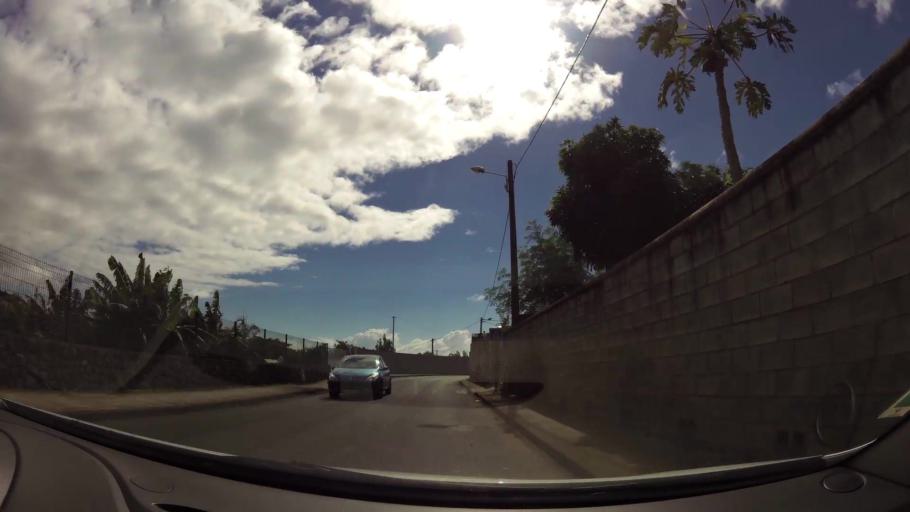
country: RE
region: Reunion
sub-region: Reunion
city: Saint-Denis
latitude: -20.9235
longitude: 55.4904
